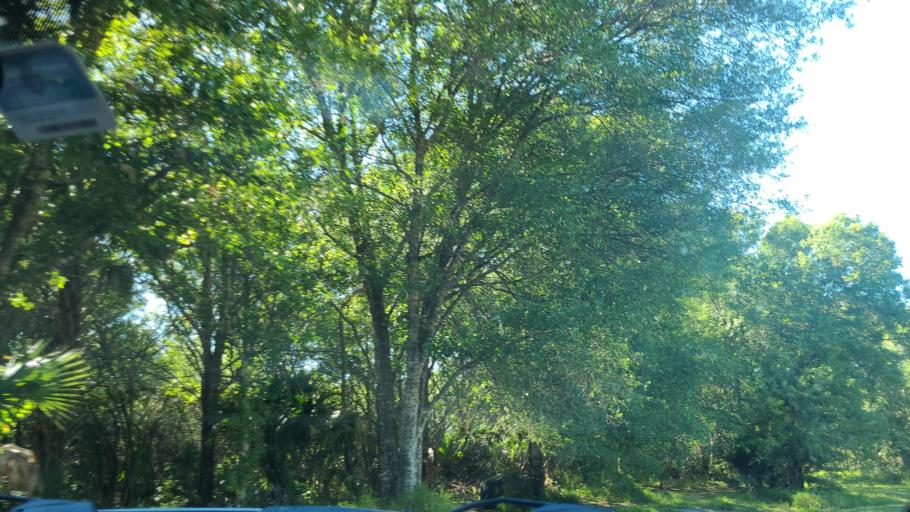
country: US
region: Florida
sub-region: Indian River County
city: Sebastian
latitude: 27.7544
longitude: -80.4824
